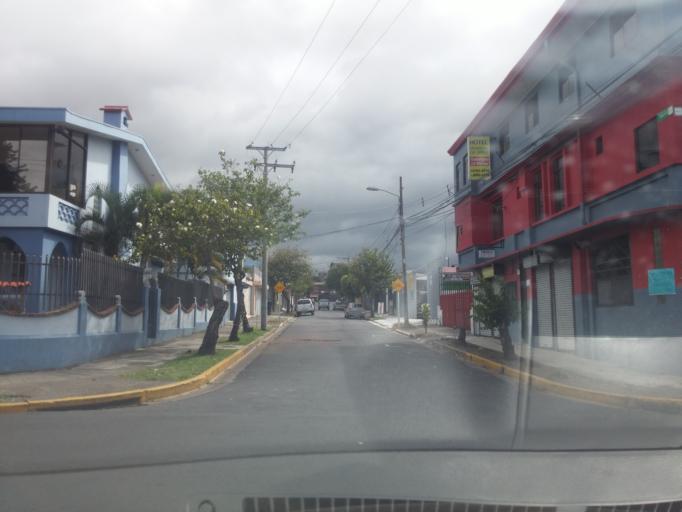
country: CR
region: San Jose
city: San Jose
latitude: 9.9341
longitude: -84.0890
